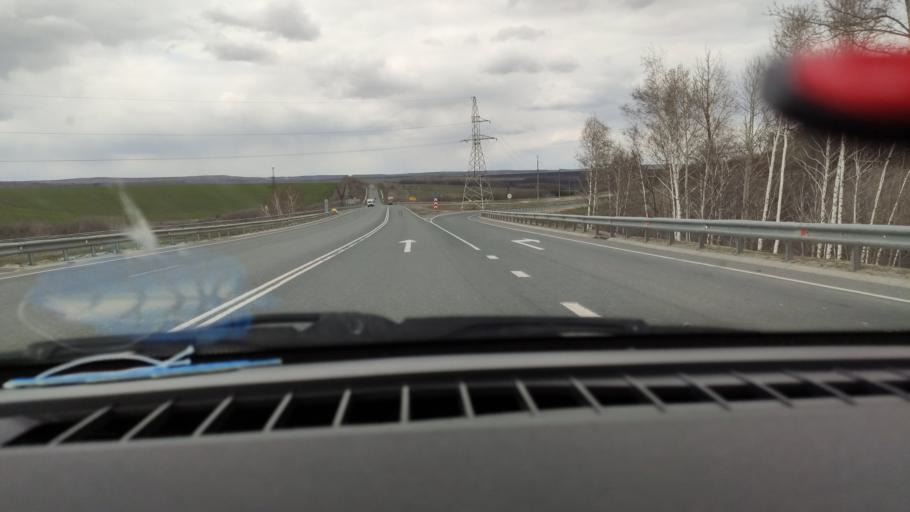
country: RU
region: Saratov
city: Shikhany
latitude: 52.1150
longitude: 47.3011
